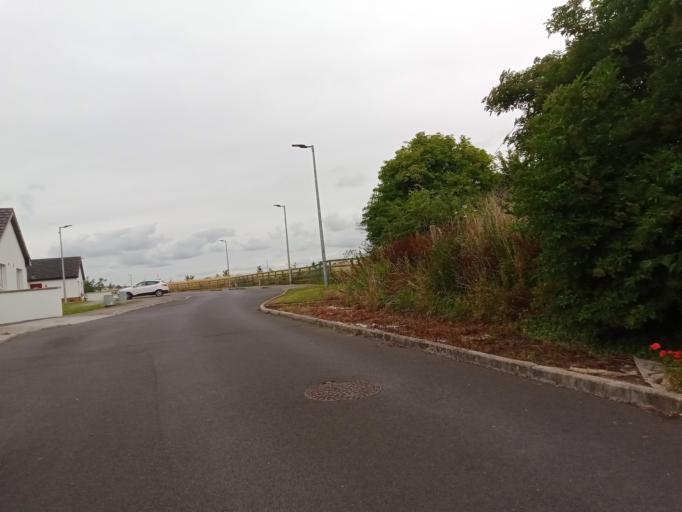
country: IE
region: Leinster
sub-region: Kilkenny
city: Callan
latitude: 52.5487
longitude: -7.3825
